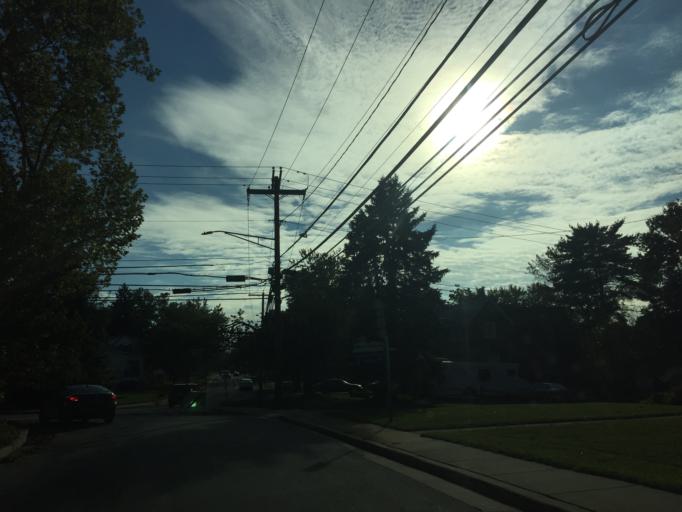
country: US
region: Maryland
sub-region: Baltimore County
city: Overlea
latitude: 39.3569
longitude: -76.5180
